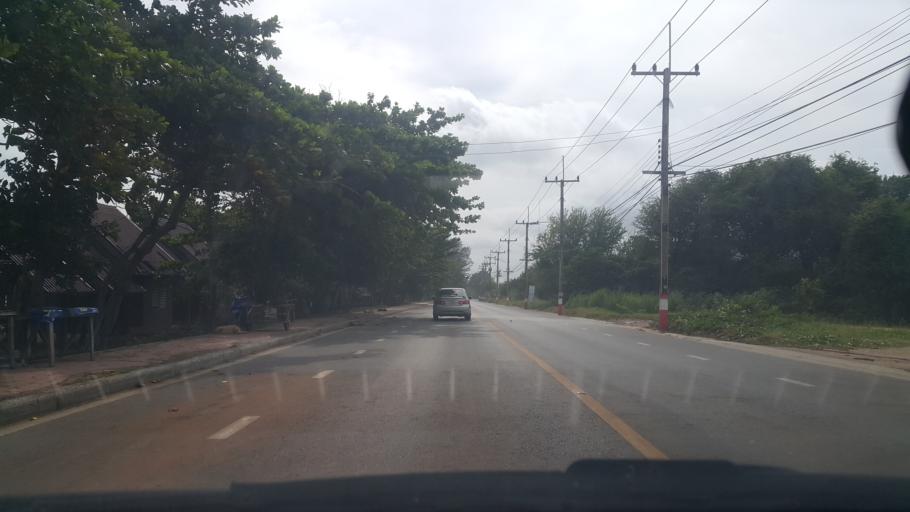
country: TH
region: Rayong
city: Rayong
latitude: 12.6301
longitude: 101.3466
